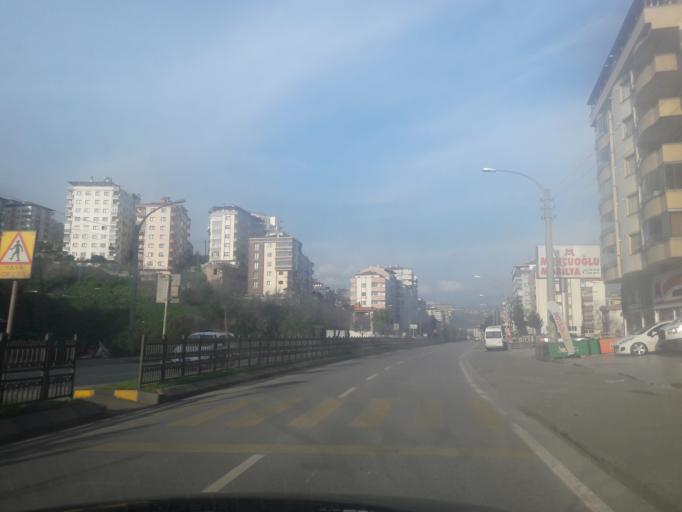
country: TR
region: Trabzon
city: Trabzon
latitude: 40.9968
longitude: 39.6868
